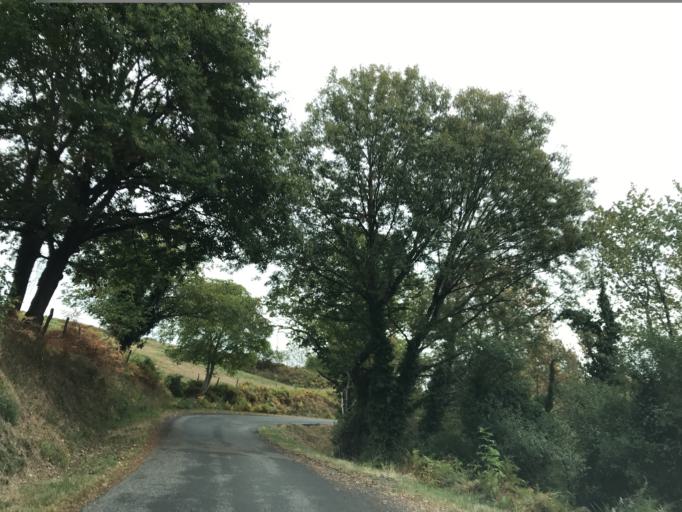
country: FR
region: Auvergne
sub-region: Departement du Puy-de-Dome
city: Thiers
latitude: 45.8377
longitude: 3.5598
